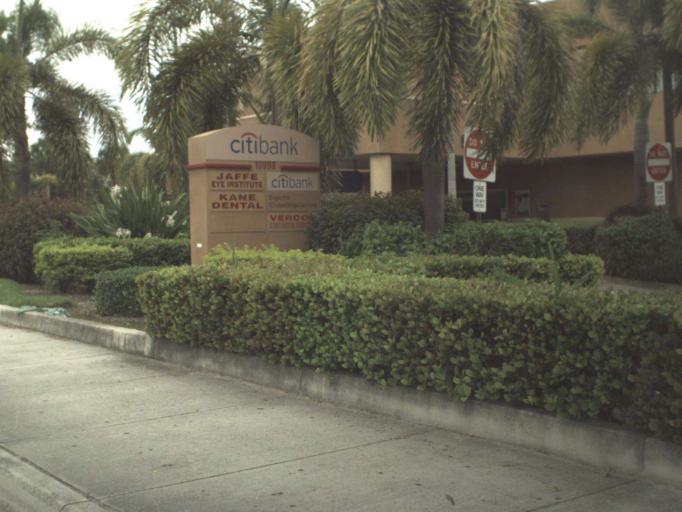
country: US
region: Florida
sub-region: Miami-Dade County
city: Ojus
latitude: 25.9502
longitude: -80.1465
